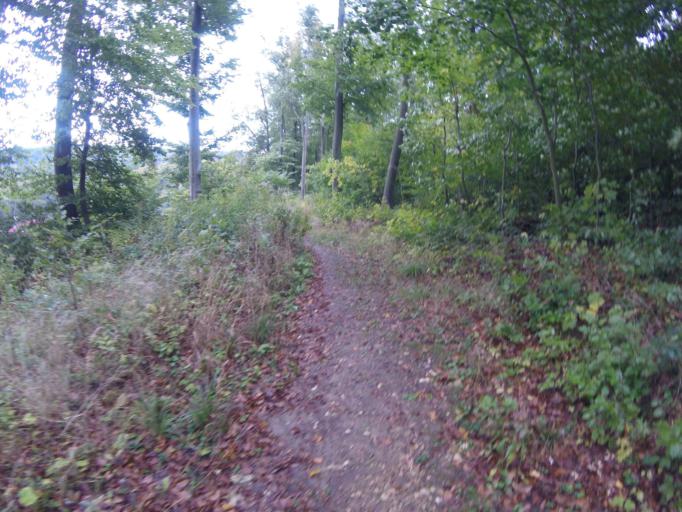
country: HU
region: Pest
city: Pilisszentkereszt
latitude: 47.7198
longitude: 18.8595
